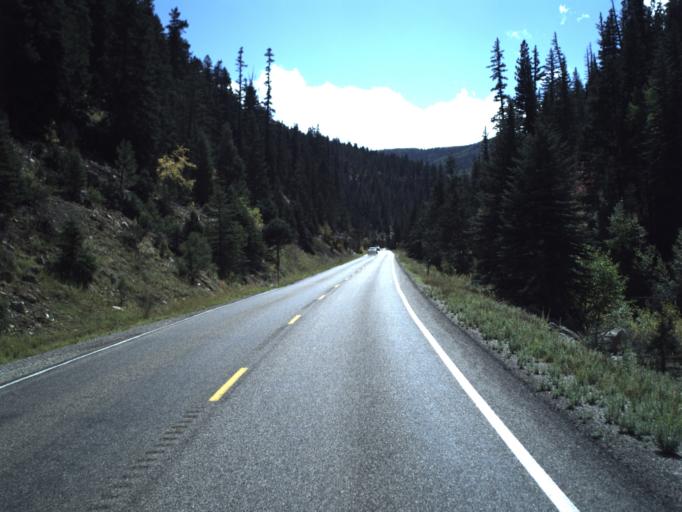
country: US
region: Utah
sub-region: Iron County
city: Cedar City
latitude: 37.6160
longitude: -112.9320
